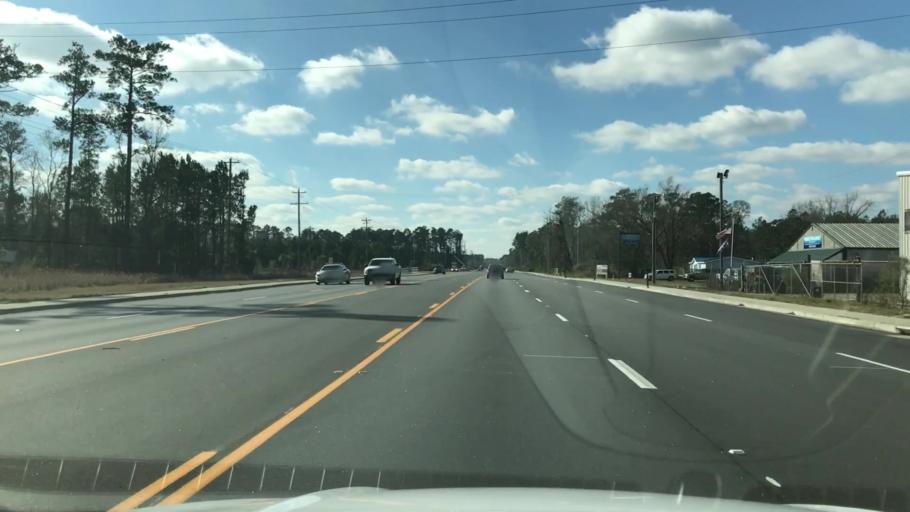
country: US
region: South Carolina
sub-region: Horry County
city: Socastee
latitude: 33.6519
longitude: -79.0207
